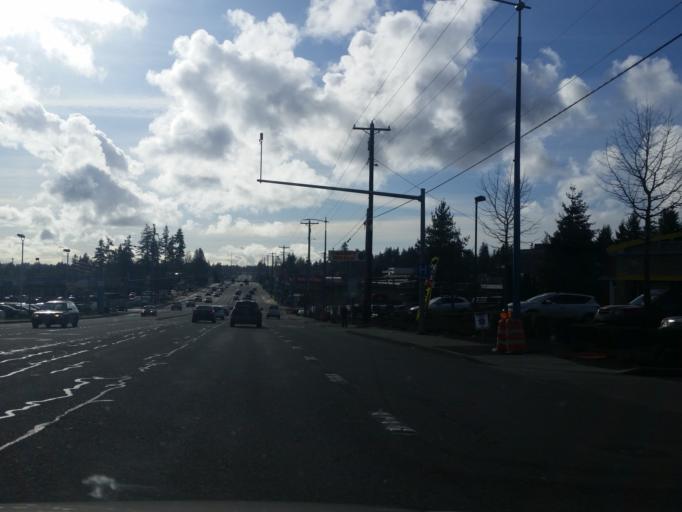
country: US
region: Washington
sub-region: Snohomish County
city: Lynnwood
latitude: 47.8048
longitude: -122.3282
